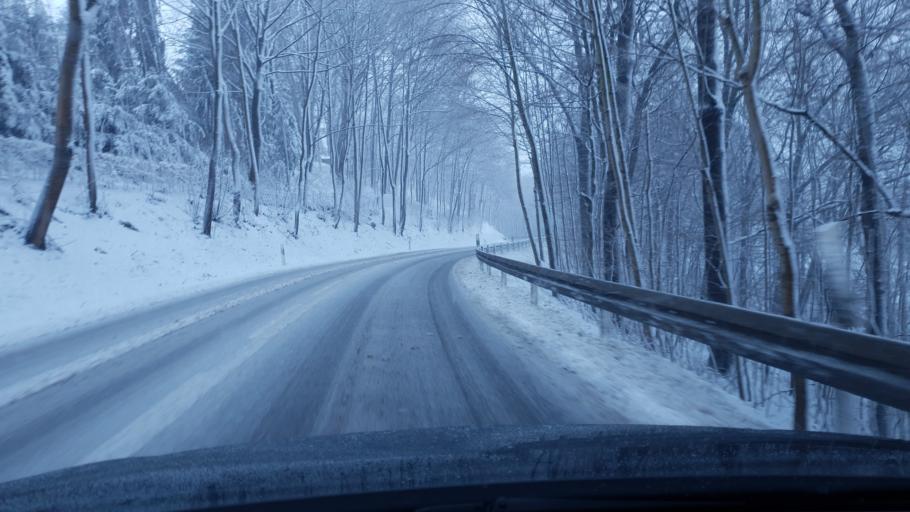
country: DE
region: Saxony
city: Wittgensdorf
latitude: 50.9007
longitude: 12.9001
